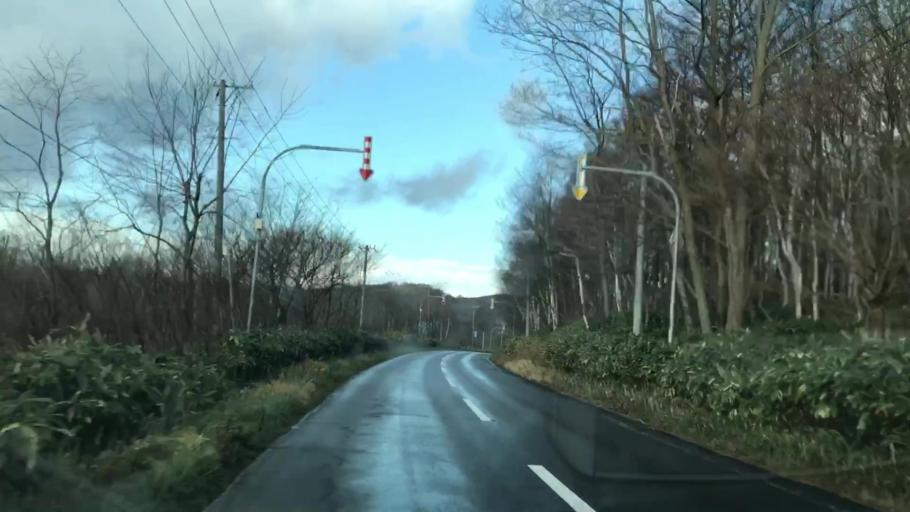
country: JP
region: Hokkaido
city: Yoichi
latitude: 43.3215
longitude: 140.5174
